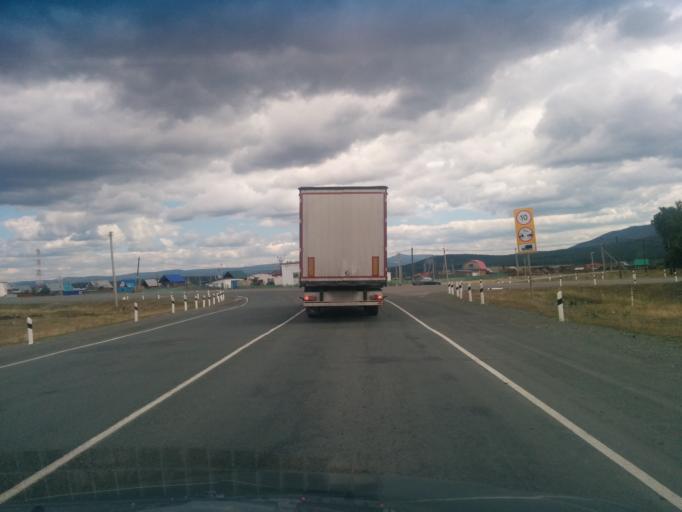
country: RU
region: Bashkortostan
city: Lomovka
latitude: 53.8803
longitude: 58.1077
